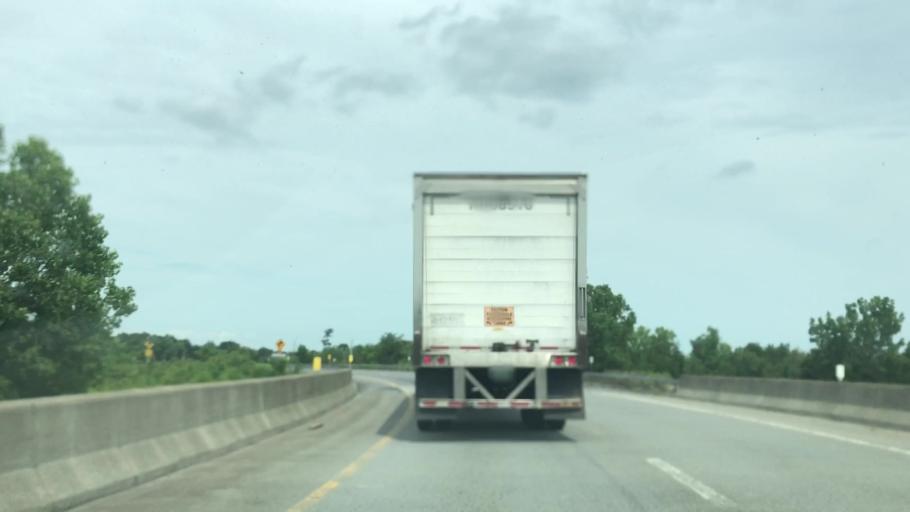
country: US
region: New York
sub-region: Albany County
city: McKownville
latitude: 42.6950
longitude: -73.8354
